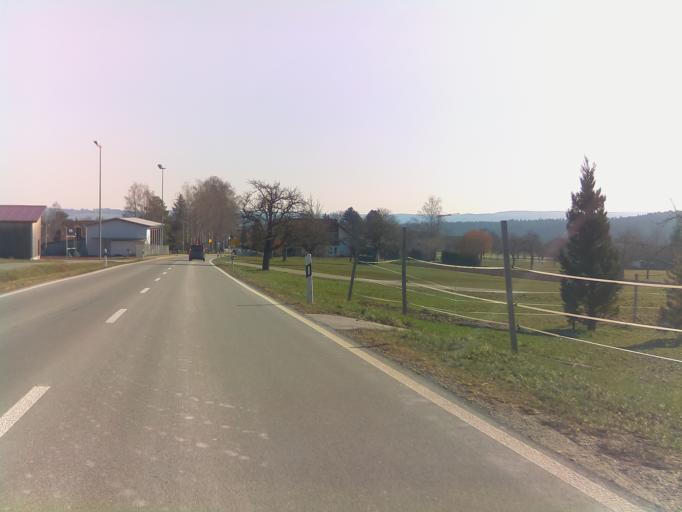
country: DE
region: Baden-Wuerttemberg
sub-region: Karlsruhe Region
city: Neubulach
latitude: 48.6527
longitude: 8.6718
